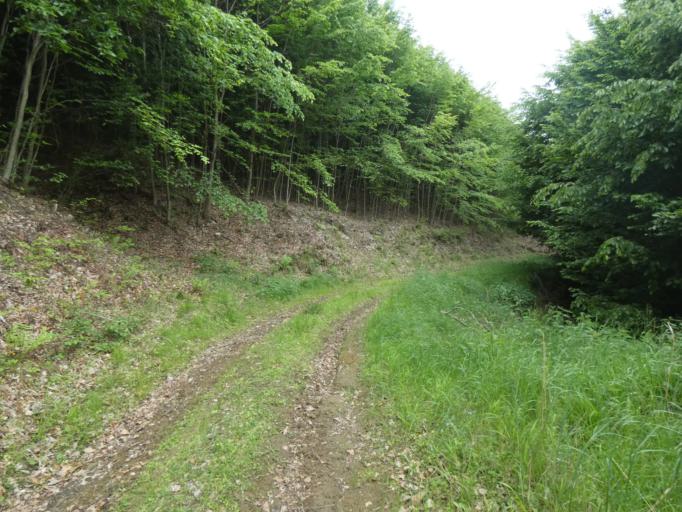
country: HU
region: Heves
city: Petervasara
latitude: 48.1159
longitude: 20.1004
